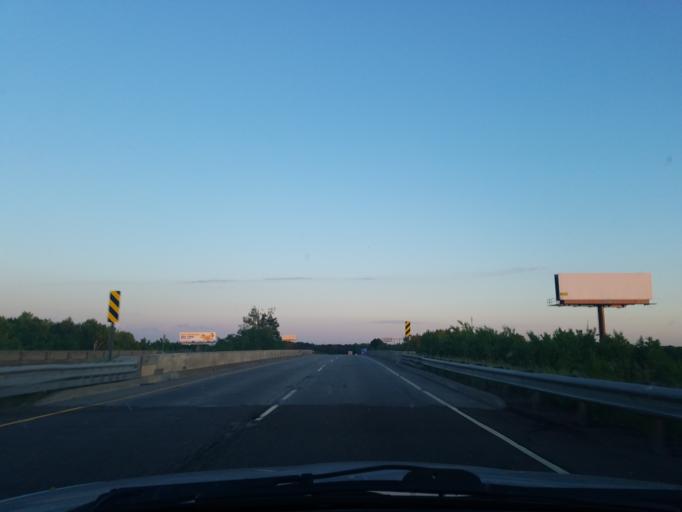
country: US
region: Minnesota
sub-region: Pine County
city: Hinckley
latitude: 46.0279
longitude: -92.9252
